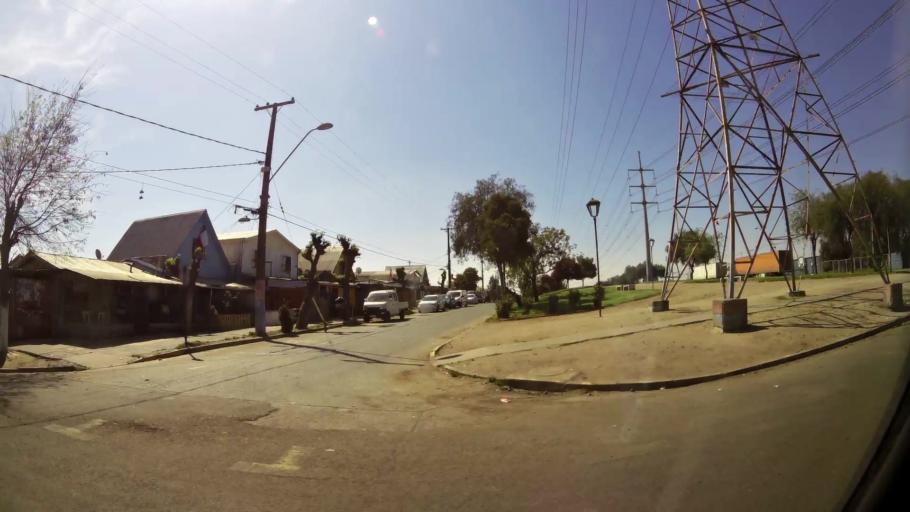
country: CL
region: Santiago Metropolitan
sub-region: Provincia de Santiago
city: Lo Prado
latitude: -33.5018
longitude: -70.7343
